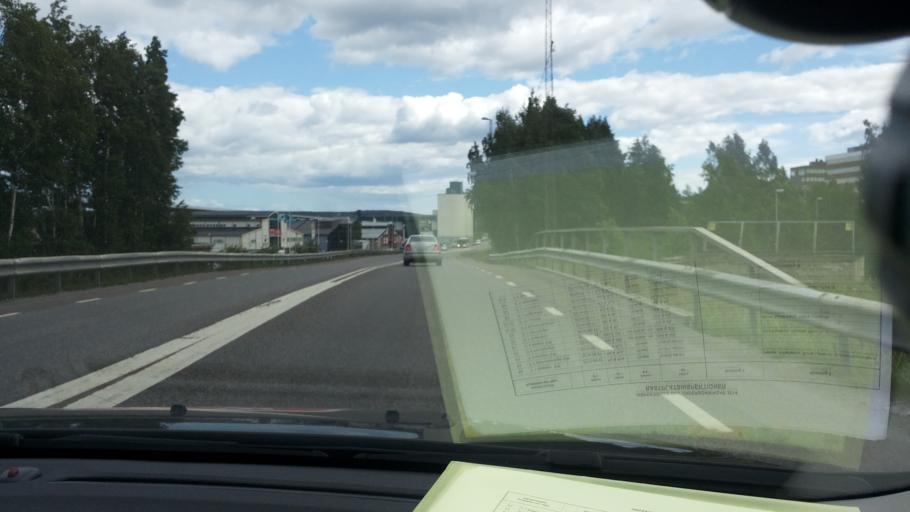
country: SE
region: Vaesternorrland
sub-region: Sundsvalls Kommun
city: Sundsvall
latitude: 62.3853
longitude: 17.3286
